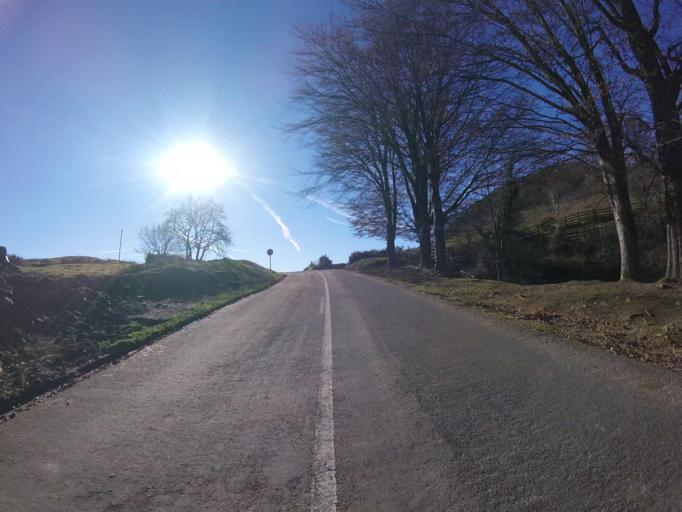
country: ES
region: Basque Country
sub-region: Provincia de Guipuzcoa
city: Irun
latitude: 43.3062
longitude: -1.7560
